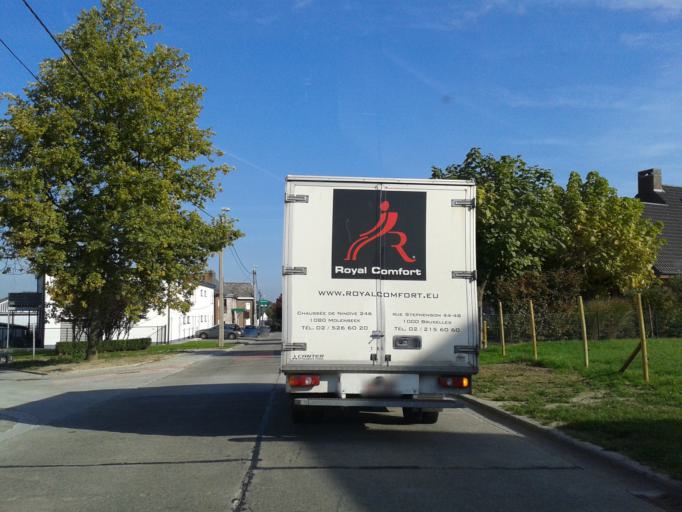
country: BE
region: Flanders
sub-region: Provincie Oost-Vlaanderen
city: Lebbeke
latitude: 50.9573
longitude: 4.1070
